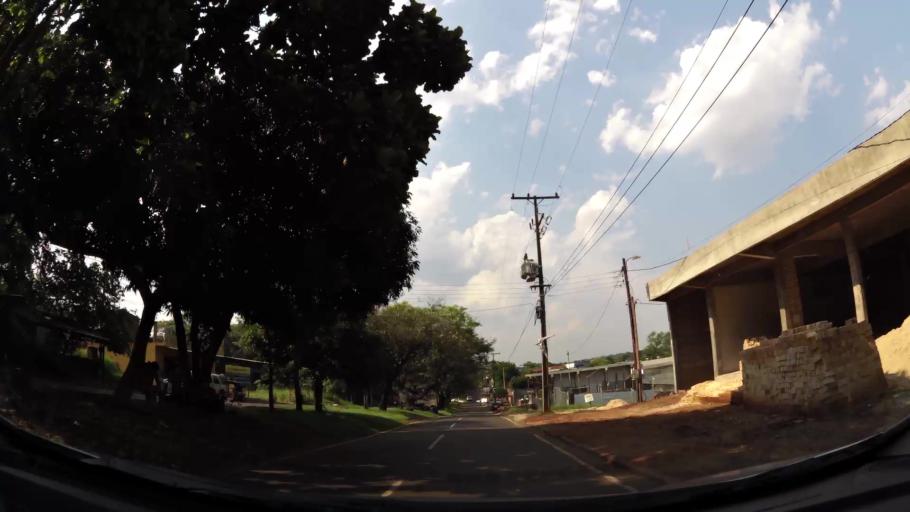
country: PY
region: Alto Parana
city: Ciudad del Este
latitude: -25.5053
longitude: -54.6291
